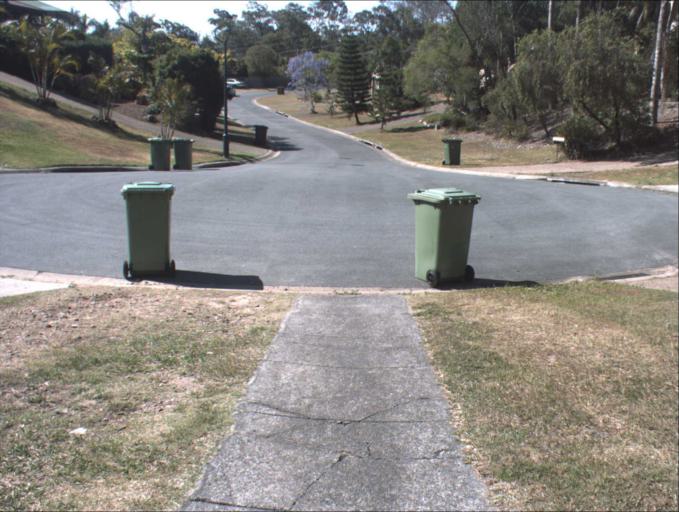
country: AU
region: Queensland
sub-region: Logan
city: Windaroo
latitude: -27.7271
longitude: 153.1862
